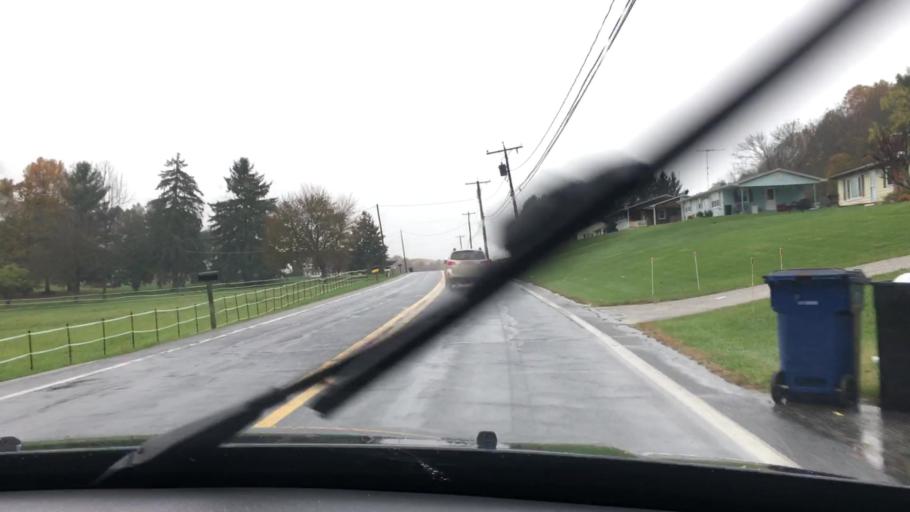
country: US
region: Maryland
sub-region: Carroll County
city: Manchester
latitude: 39.6899
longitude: -76.8790
